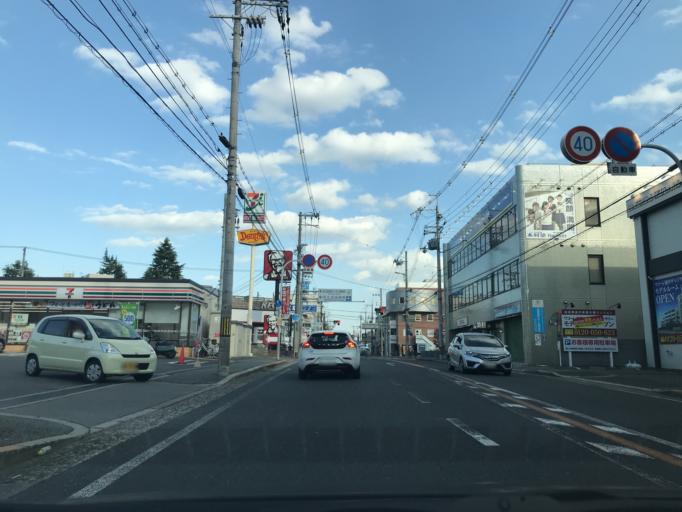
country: JP
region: Osaka
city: Ikeda
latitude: 34.8194
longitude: 135.4308
